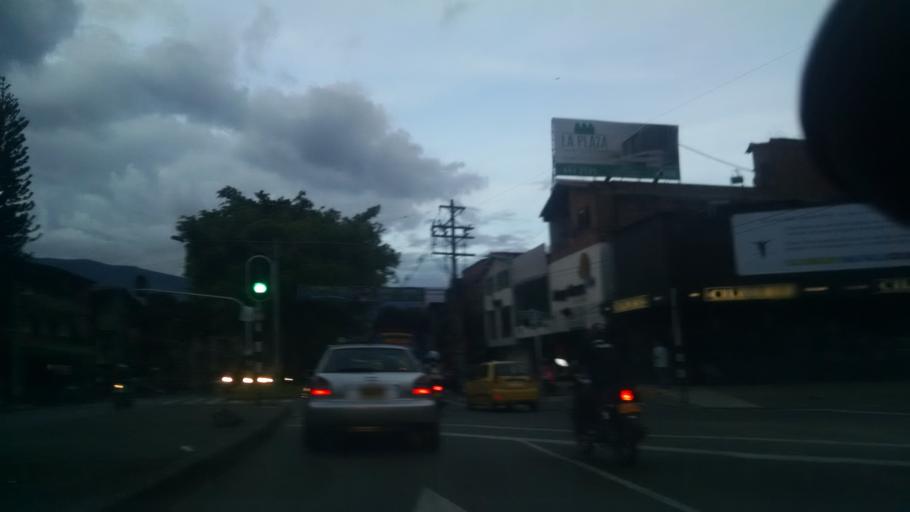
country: CO
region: Antioquia
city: Itagui
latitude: 6.2271
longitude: -75.6018
